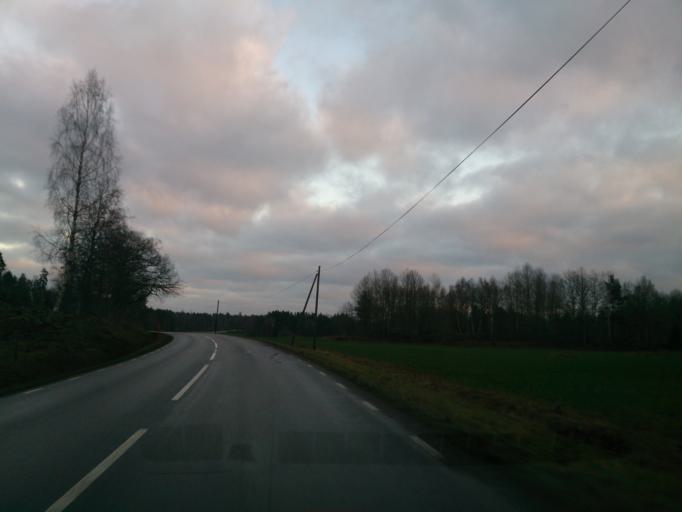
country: SE
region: OEstergoetland
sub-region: Norrkopings Kommun
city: Kimstad
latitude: 58.3903
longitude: 15.9764
